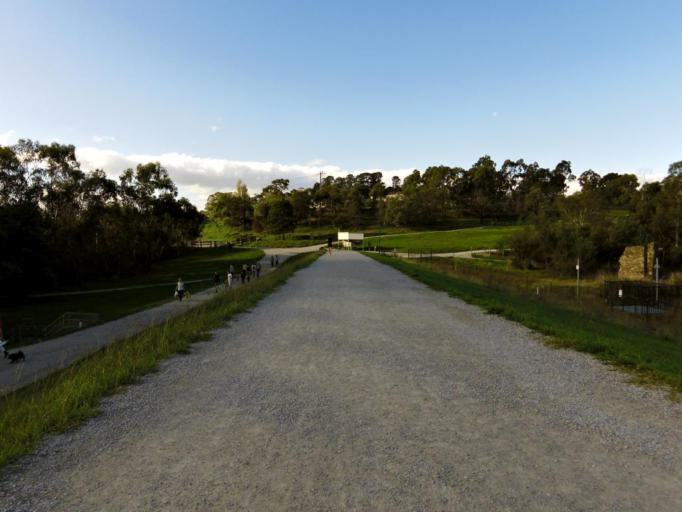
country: AU
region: Victoria
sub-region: Yarra Ranges
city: Lilydale
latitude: -37.7629
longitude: 145.3522
